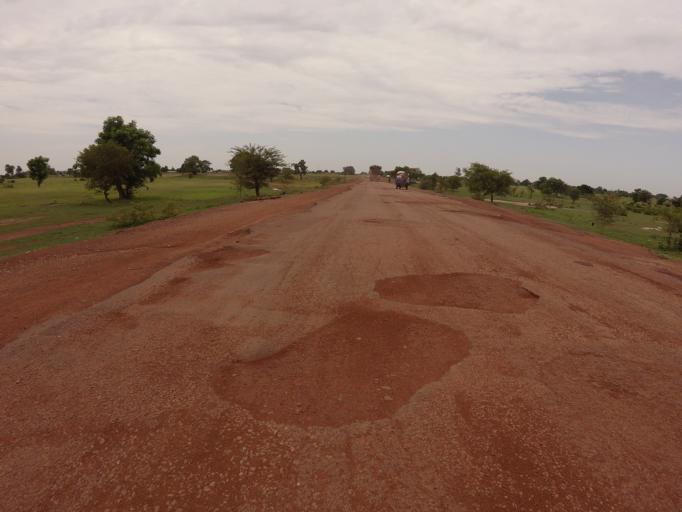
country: GH
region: Upper East
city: Bawku
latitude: 11.0024
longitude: -0.3804
